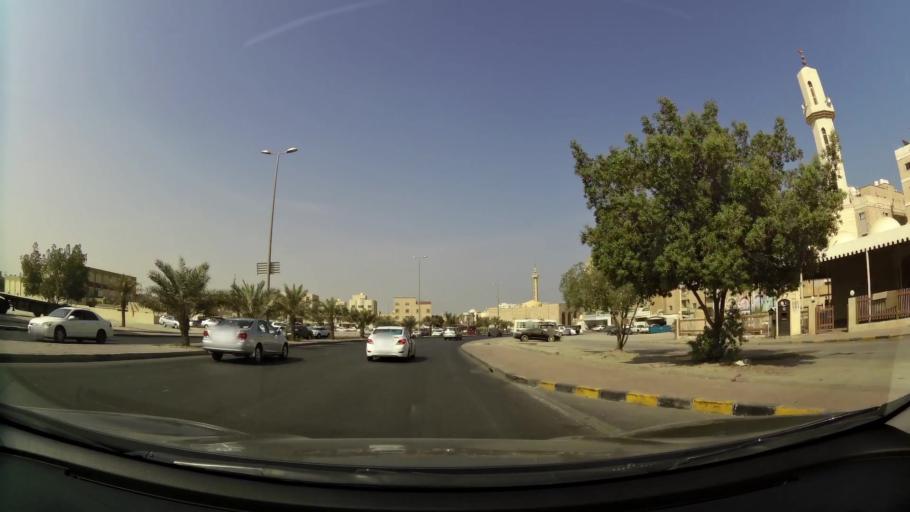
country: KW
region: Al Ahmadi
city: Al Manqaf
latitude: 29.1052
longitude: 48.1240
